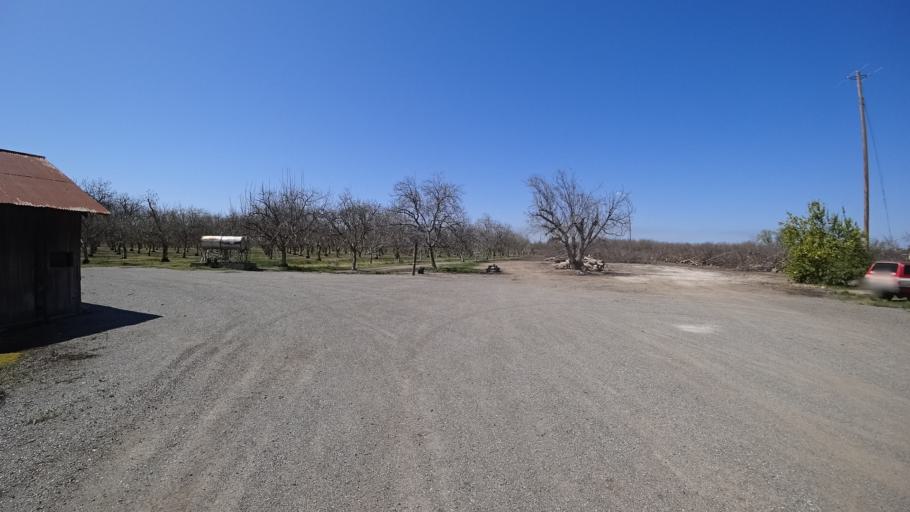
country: US
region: California
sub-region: Glenn County
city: Willows
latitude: 39.4480
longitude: -121.9888
